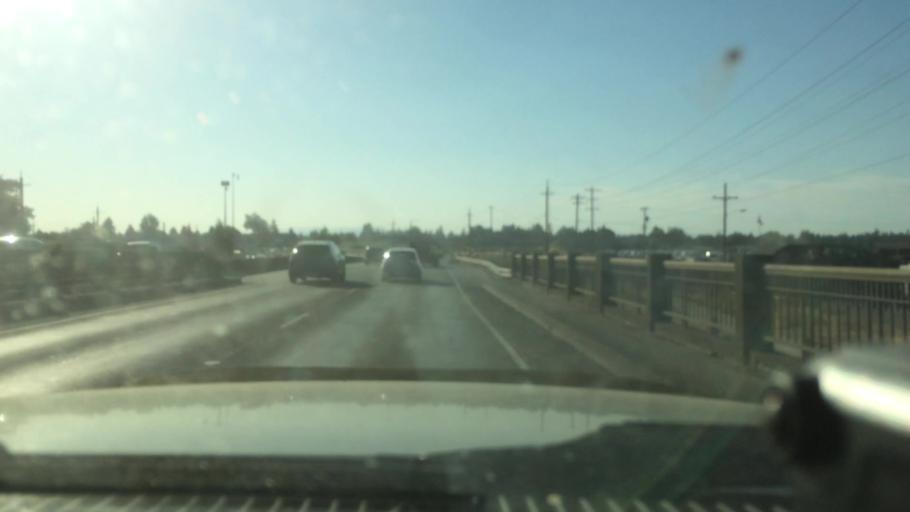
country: US
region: Oregon
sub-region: Lane County
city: Eugene
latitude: 44.0957
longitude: -123.1074
